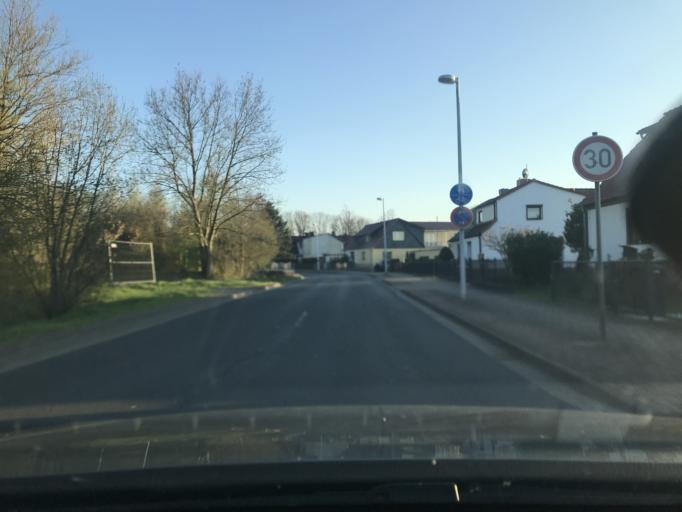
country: DE
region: Thuringia
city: Nordhausen
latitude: 51.4947
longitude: 10.7704
